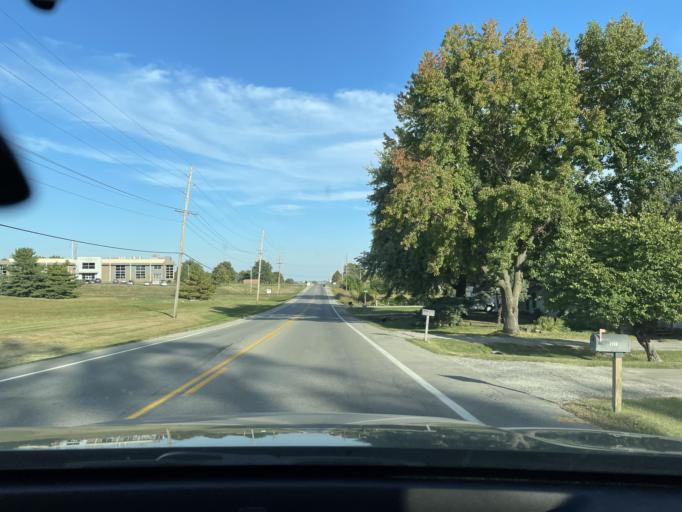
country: US
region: Missouri
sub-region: Buchanan County
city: Saint Joseph
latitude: 39.7552
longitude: -94.7943
